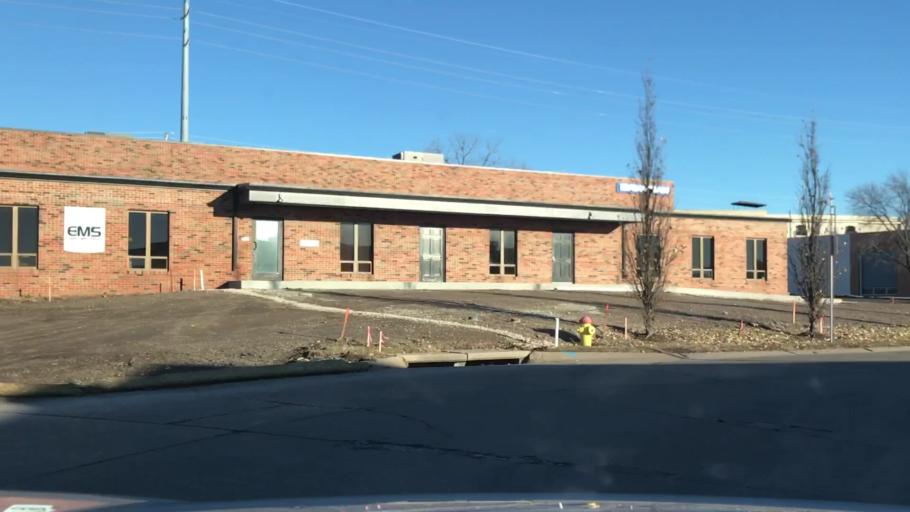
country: US
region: Missouri
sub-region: Saint Louis County
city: Brentwood
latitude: 38.6241
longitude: -90.3386
